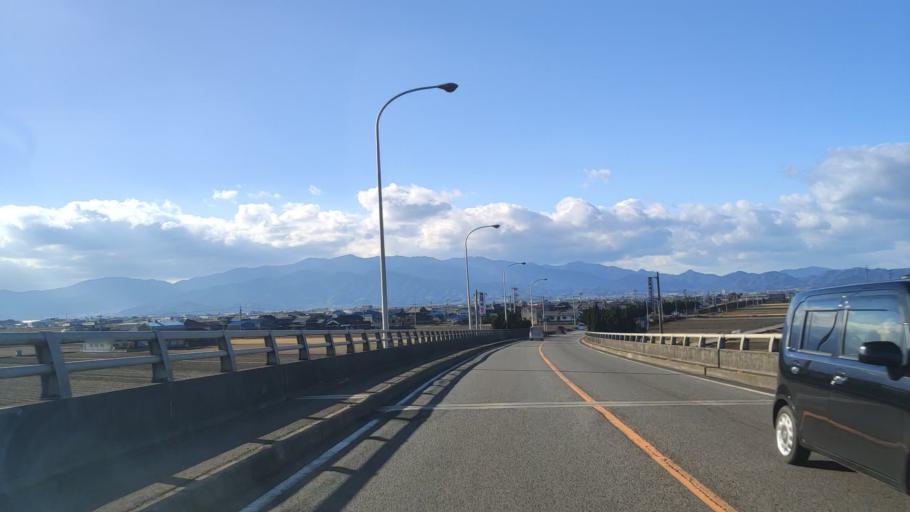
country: JP
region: Ehime
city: Saijo
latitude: 33.9159
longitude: 133.1318
